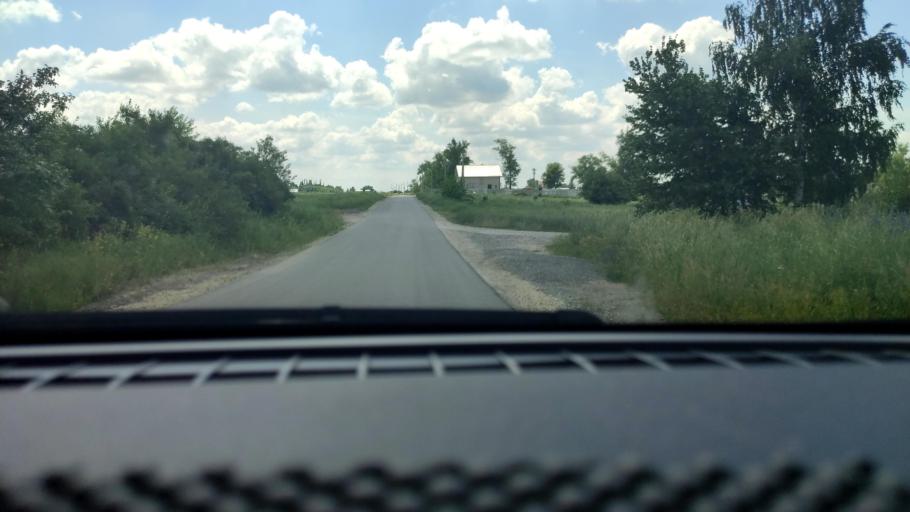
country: RU
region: Voronezj
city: Ramon'
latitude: 51.8990
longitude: 39.1765
